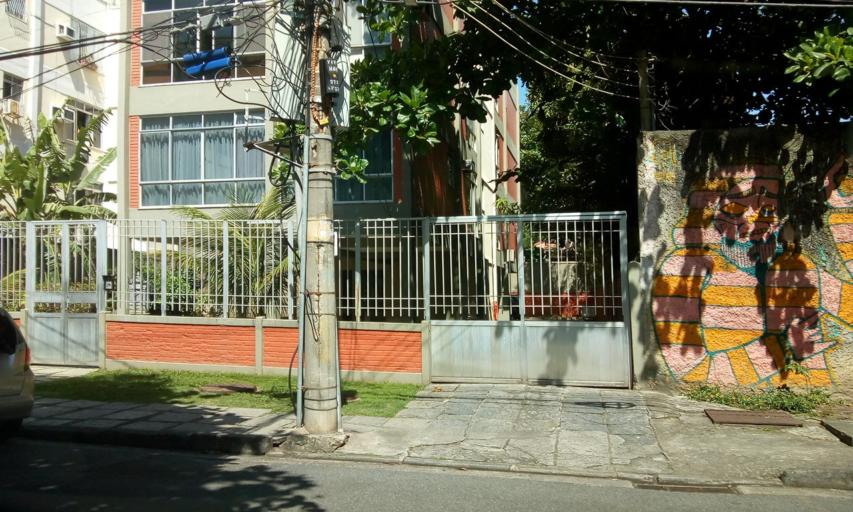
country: BR
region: Rio de Janeiro
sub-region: Rio De Janeiro
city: Rio de Janeiro
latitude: -23.0126
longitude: -43.3159
